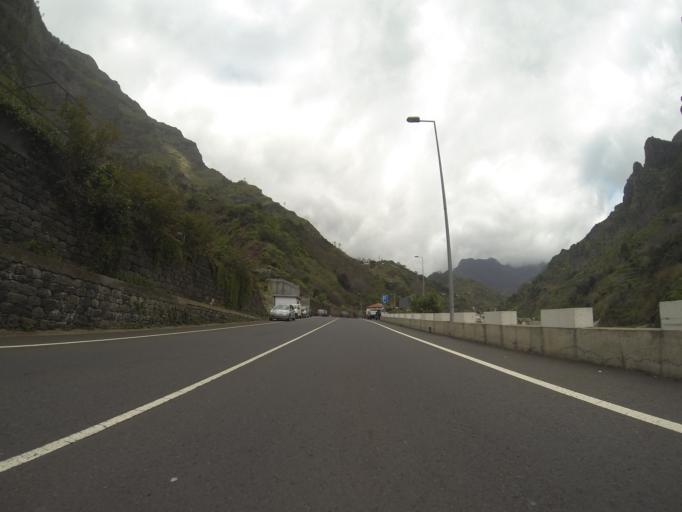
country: PT
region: Madeira
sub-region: Ribeira Brava
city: Campanario
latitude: 32.7204
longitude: -17.0310
